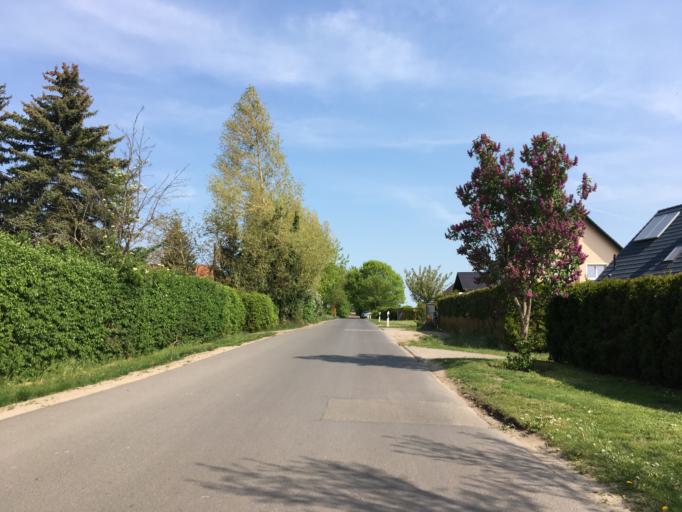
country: DE
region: Brandenburg
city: Altlandsberg
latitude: 52.5817
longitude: 13.7255
